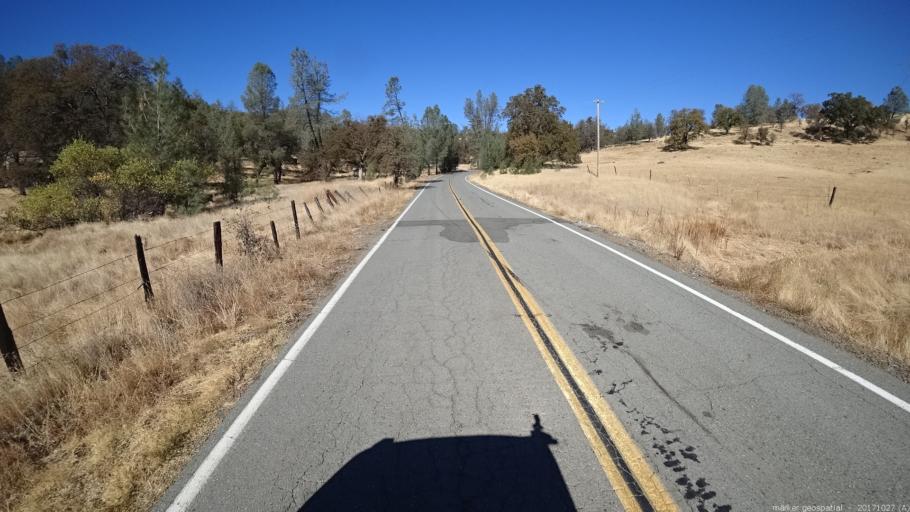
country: US
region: California
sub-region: Shasta County
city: Bella Vista
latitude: 40.7049
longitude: -122.0403
